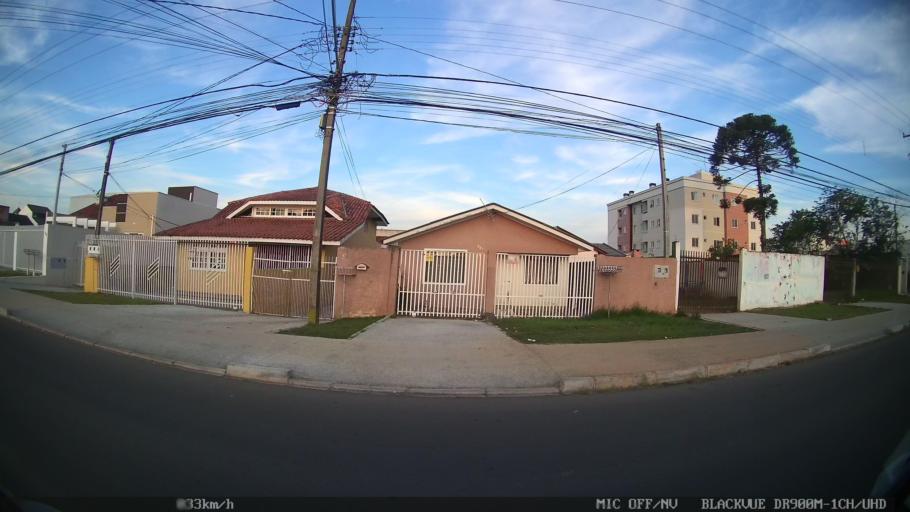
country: BR
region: Parana
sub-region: Pinhais
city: Pinhais
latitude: -25.4557
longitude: -49.1829
